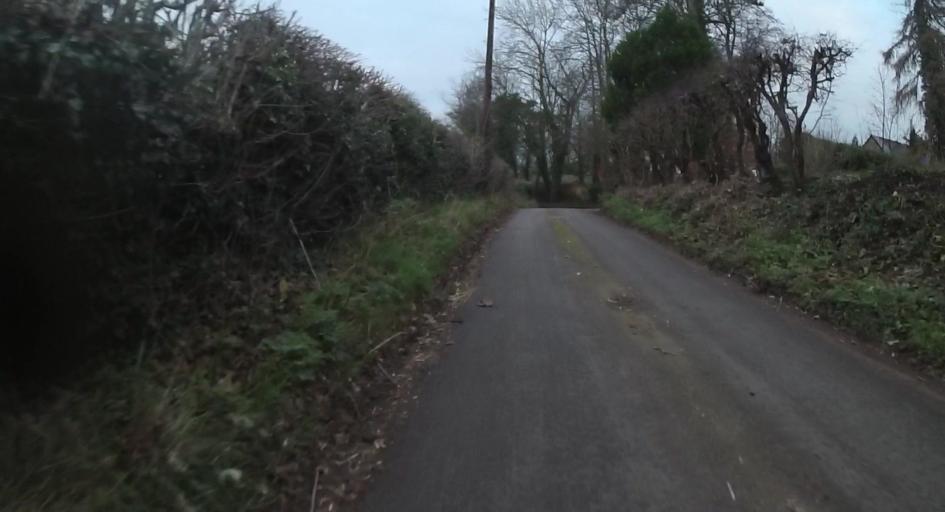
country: GB
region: England
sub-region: Surrey
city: Farnham
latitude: 51.2127
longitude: -0.8361
